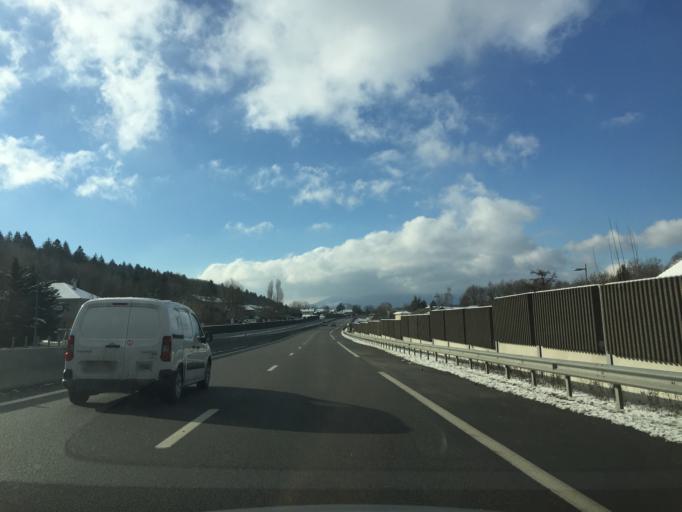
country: FR
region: Rhone-Alpes
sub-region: Departement de la Haute-Savoie
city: Saint-Cergues
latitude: 46.2182
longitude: 6.3072
